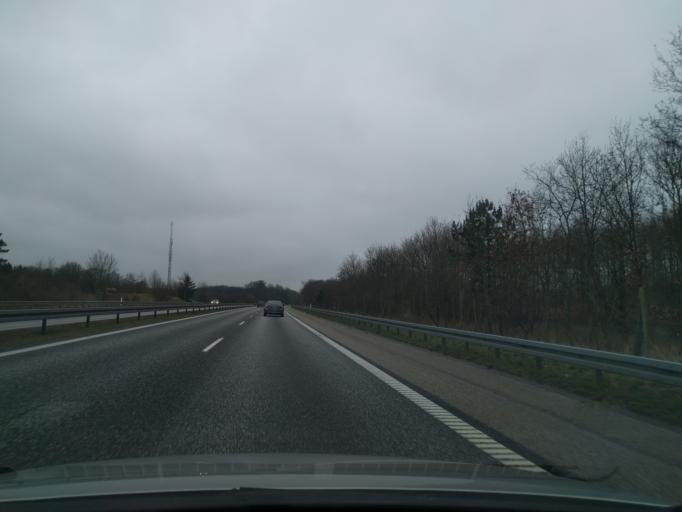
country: DK
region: Zealand
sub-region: Soro Kommune
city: Soro
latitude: 55.4436
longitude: 11.5101
